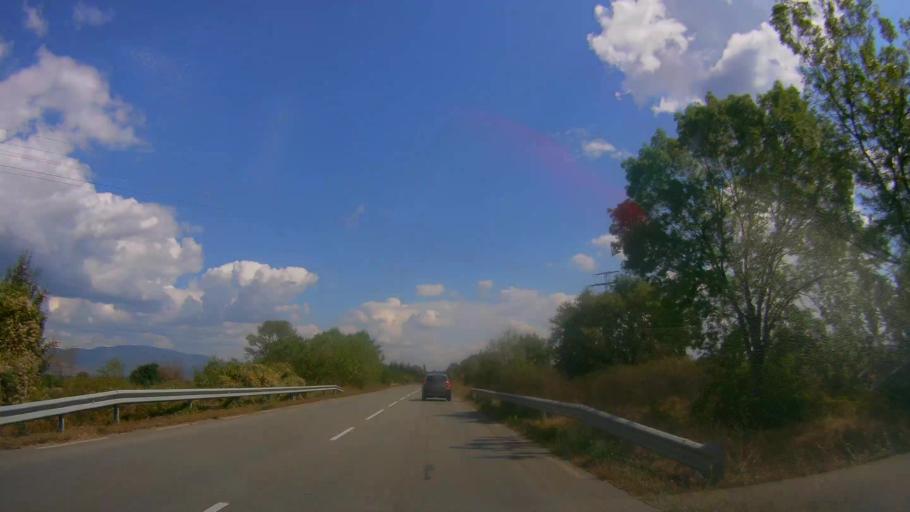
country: BG
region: Sliven
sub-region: Obshtina Tvurditsa
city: Tvurditsa
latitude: 42.6528
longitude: 25.9674
